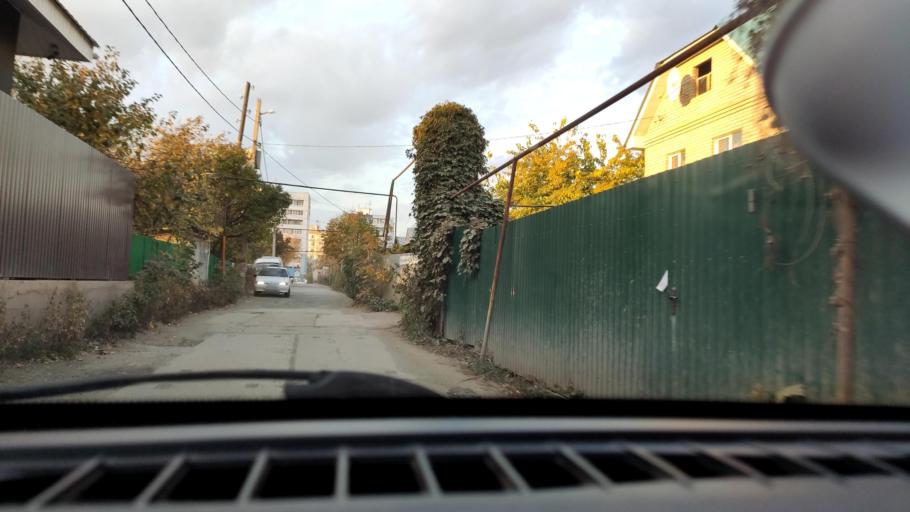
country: RU
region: Samara
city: Samara
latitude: 53.2687
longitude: 50.2288
